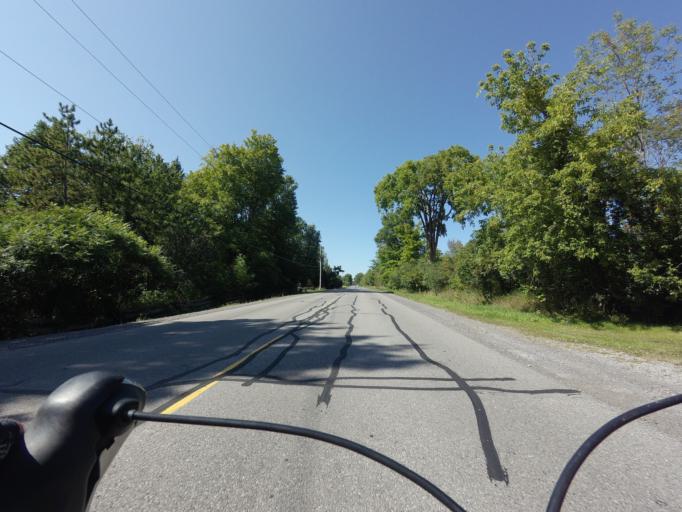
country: CA
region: Ontario
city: Bells Corners
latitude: 45.4156
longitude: -75.9398
